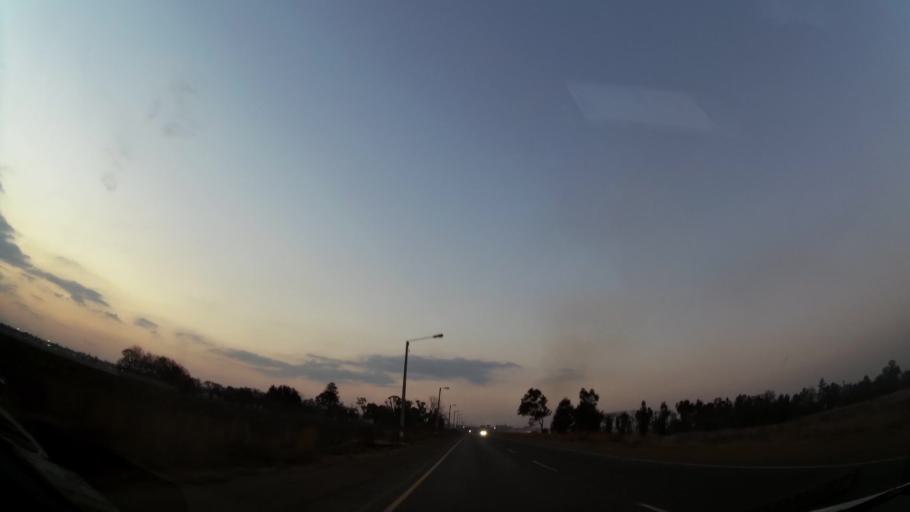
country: ZA
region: Gauteng
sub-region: Ekurhuleni Metropolitan Municipality
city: Springs
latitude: -26.3329
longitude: 28.4548
